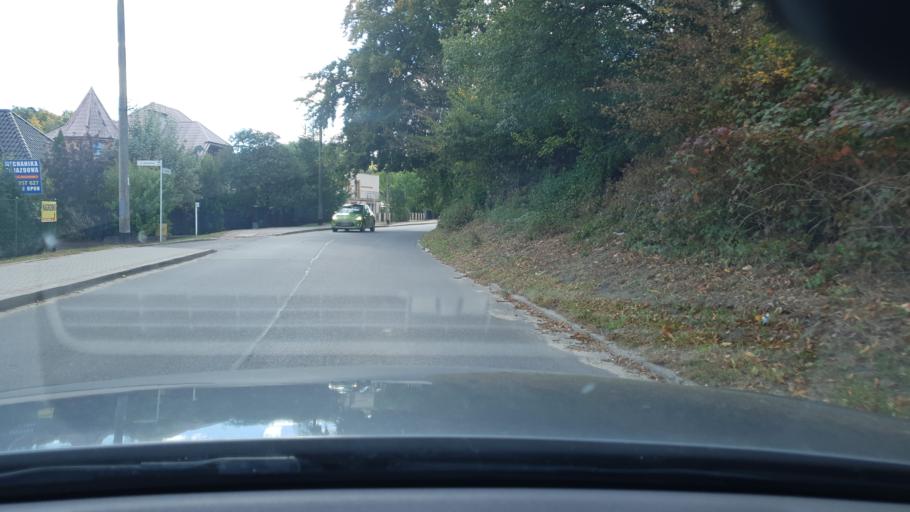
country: PL
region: Pomeranian Voivodeship
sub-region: Powiat wejherowski
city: Reda
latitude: 54.5977
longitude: 18.3458
